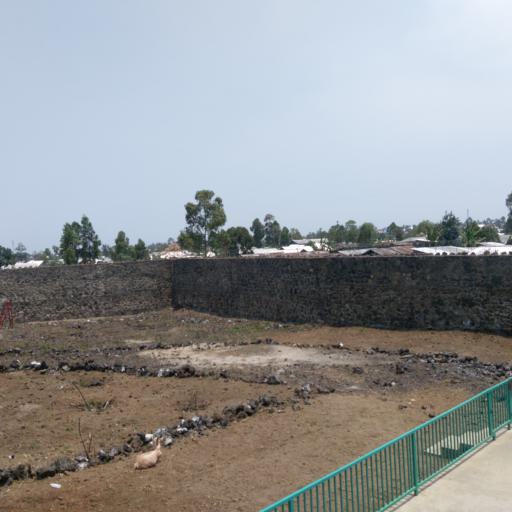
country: CD
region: Nord Kivu
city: Goma
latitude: -1.6451
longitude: 29.2311
